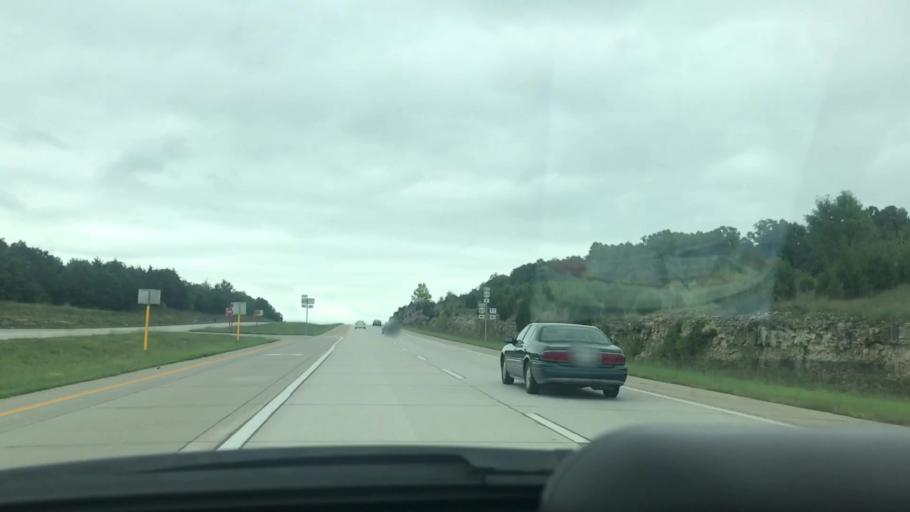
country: US
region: Missouri
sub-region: Dallas County
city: Buffalo
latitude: 37.5184
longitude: -93.1381
